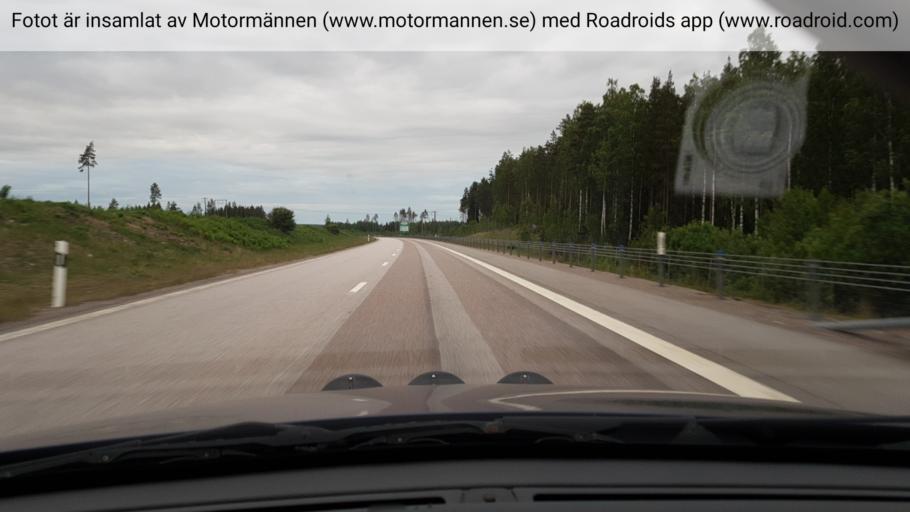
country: SE
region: Uppsala
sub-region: Tierps Kommun
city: Tierp
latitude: 60.3083
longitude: 17.5222
